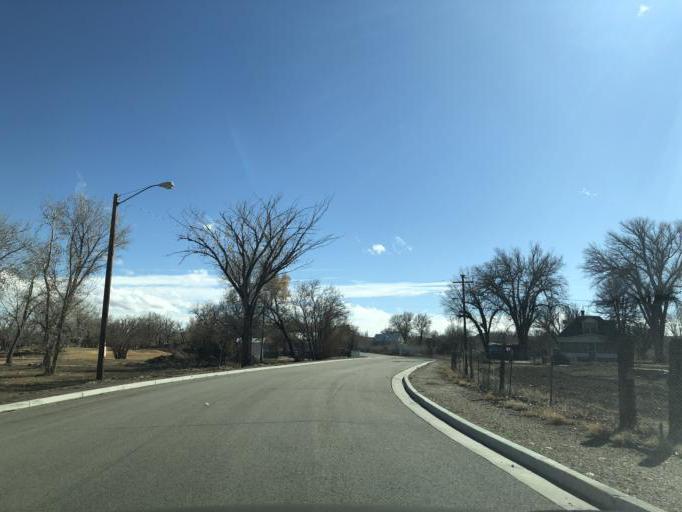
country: US
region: Utah
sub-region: Carbon County
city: East Carbon City
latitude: 38.9914
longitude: -110.1556
